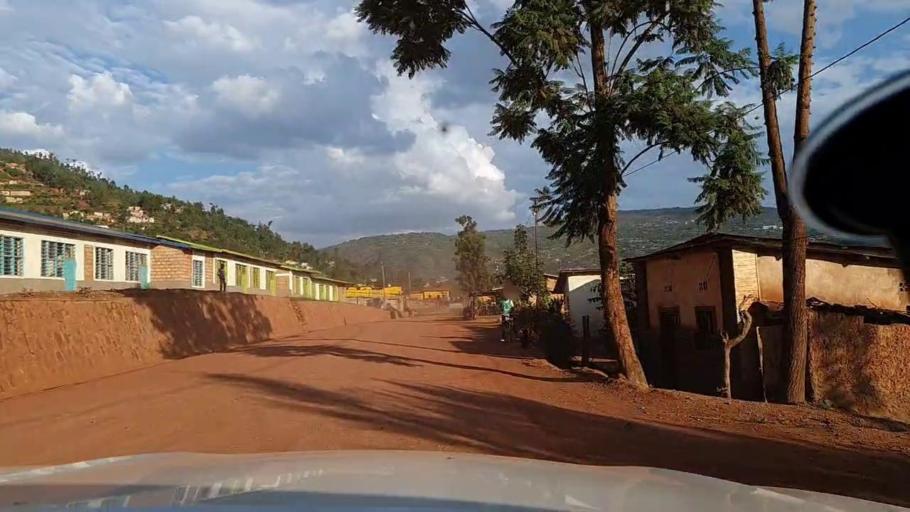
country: RW
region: Kigali
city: Kigali
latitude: -1.9441
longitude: 30.0064
